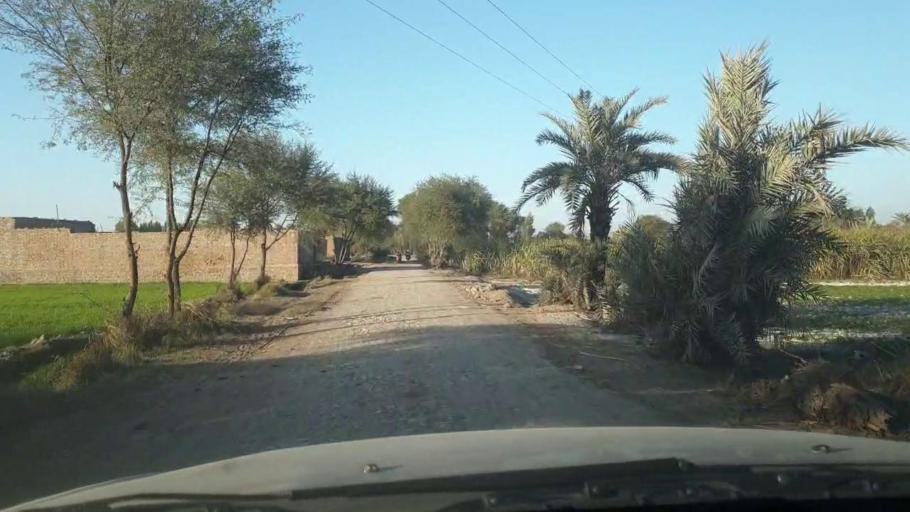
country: PK
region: Sindh
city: Ghotki
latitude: 28.0255
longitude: 69.3081
